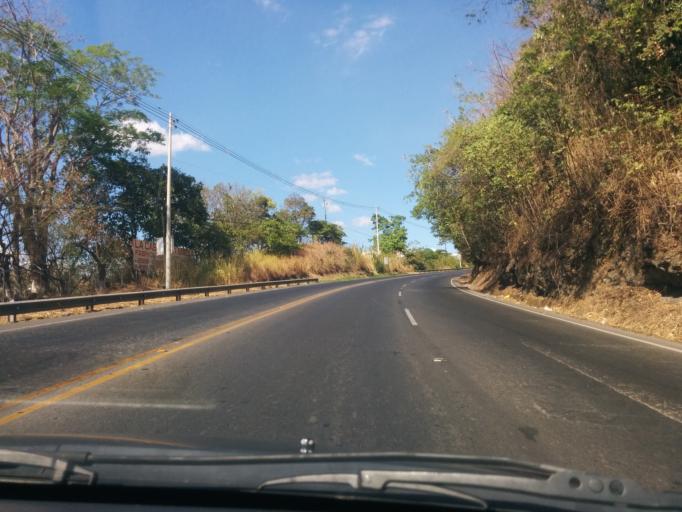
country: CR
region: Alajuela
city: Carrillos
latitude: 10.0054
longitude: -84.2979
